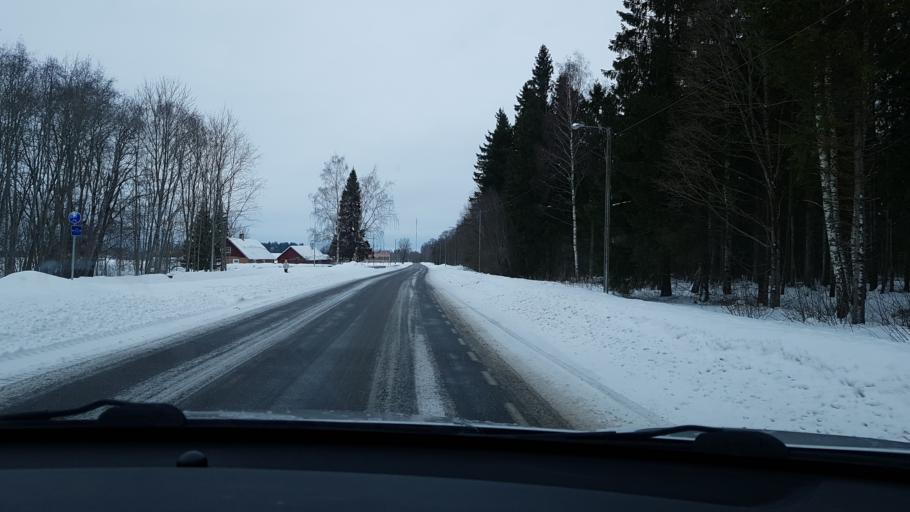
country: EE
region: Jaervamaa
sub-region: Jaerva-Jaani vald
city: Jarva-Jaani
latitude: 59.1321
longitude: 25.7447
